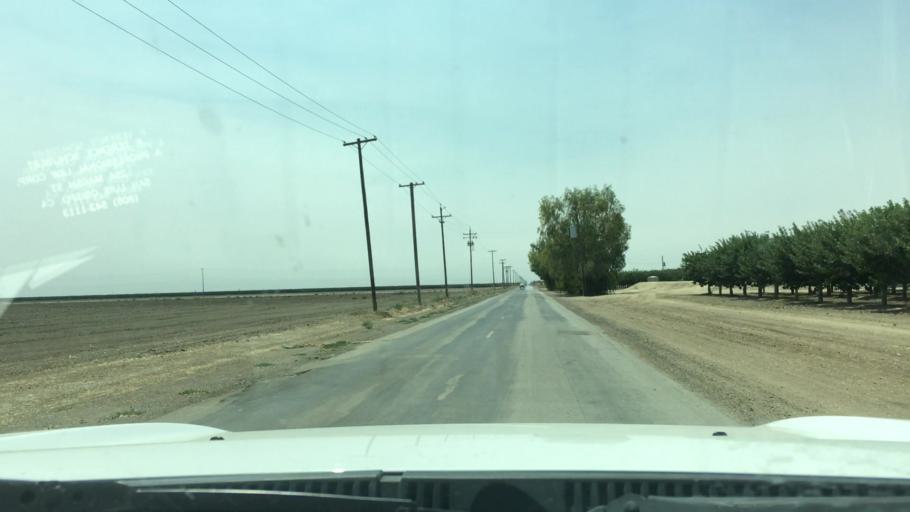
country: US
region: California
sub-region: Kern County
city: Wasco
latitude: 35.7061
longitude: -119.4373
